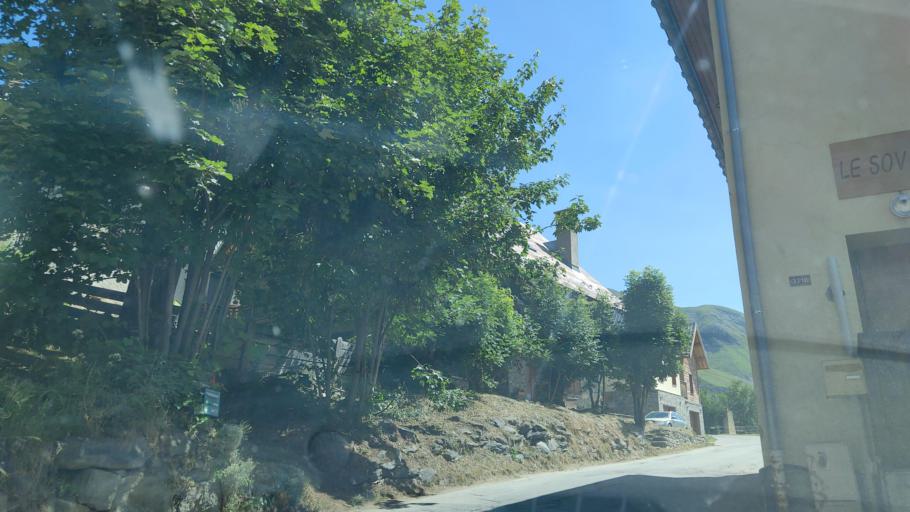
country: FR
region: Rhone-Alpes
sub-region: Departement de la Savoie
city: Saint-Jean-de-Maurienne
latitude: 45.2219
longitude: 6.2232
